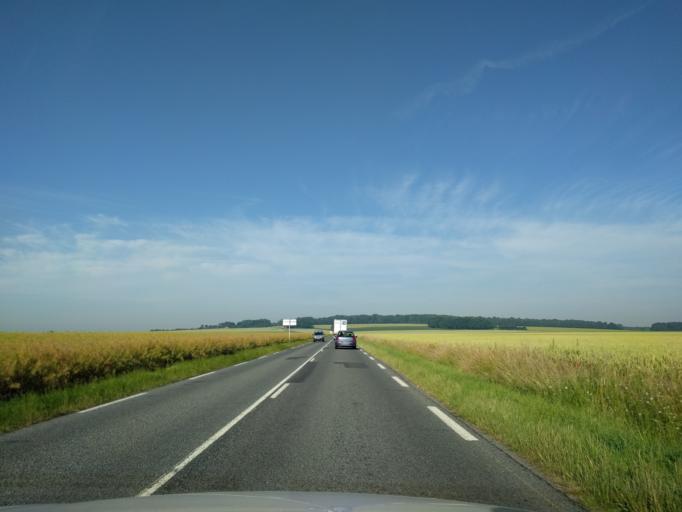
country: FR
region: Picardie
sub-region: Departement de la Somme
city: Montdidier
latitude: 49.6367
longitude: 2.4782
